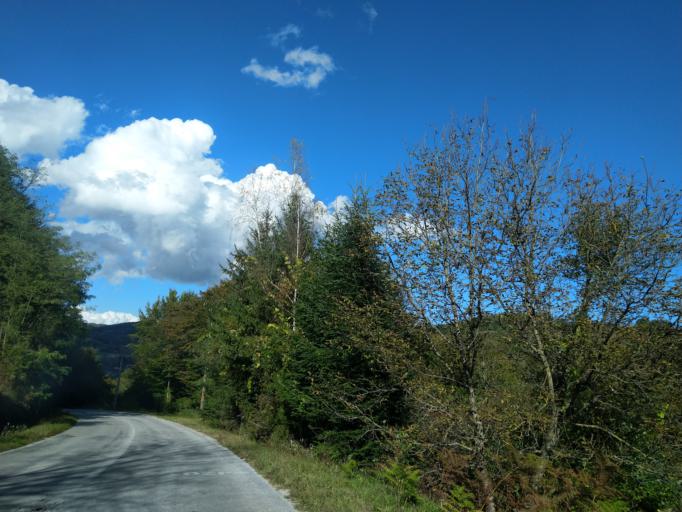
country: RS
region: Central Serbia
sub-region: Zlatiborski Okrug
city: Uzice
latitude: 43.8823
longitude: 19.7751
